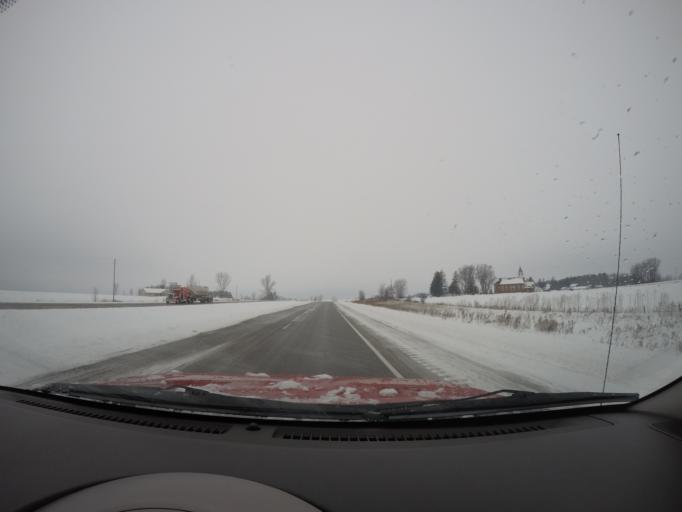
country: US
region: Minnesota
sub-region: Winona County
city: Goodview
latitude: 43.9488
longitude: -91.7068
